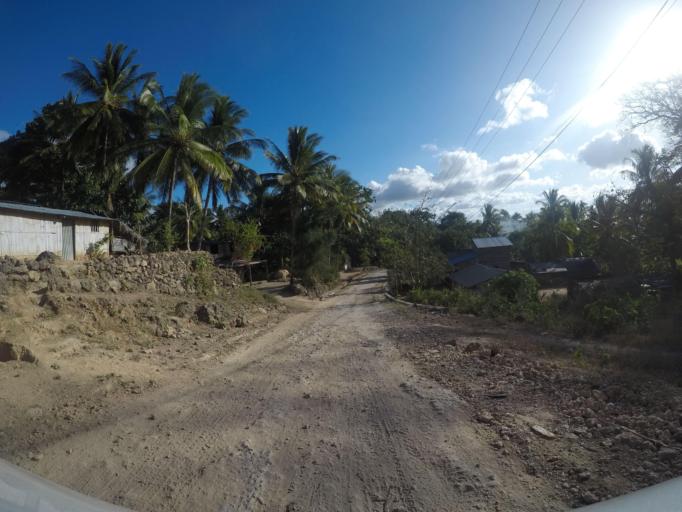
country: TL
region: Lautem
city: Lospalos
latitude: -8.4385
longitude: 126.8573
